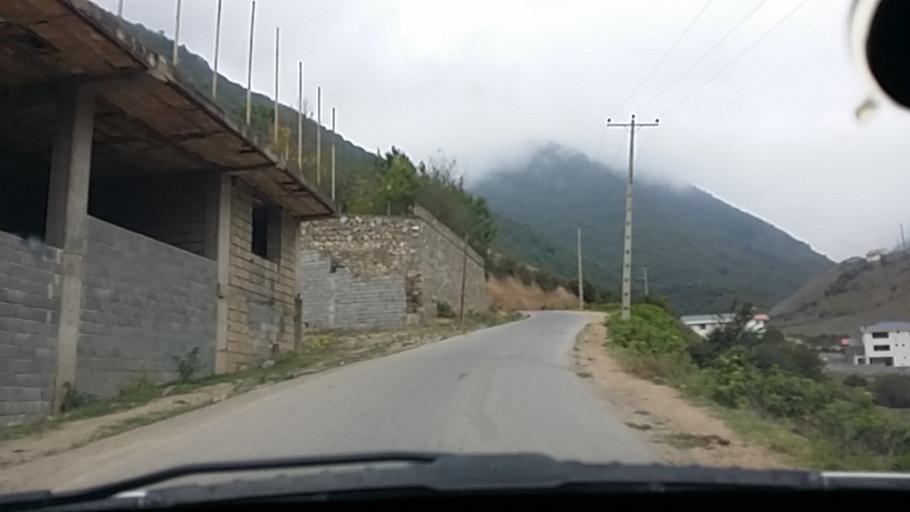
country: IR
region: Mazandaran
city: `Abbasabad
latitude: 36.4726
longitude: 51.1401
